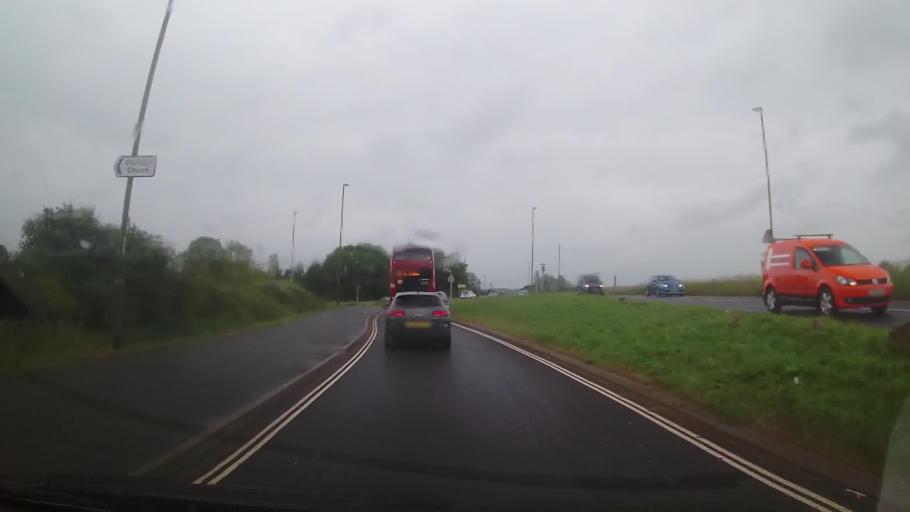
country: GB
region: England
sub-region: Borough of Torbay
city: Paignton
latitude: 50.4015
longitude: -3.5647
